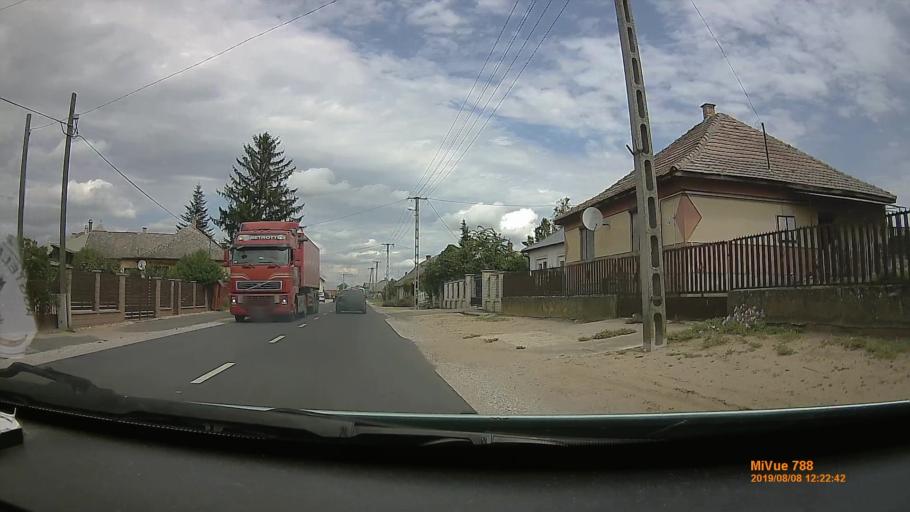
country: HU
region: Szabolcs-Szatmar-Bereg
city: Nyirbogat
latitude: 47.8001
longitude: 22.0543
